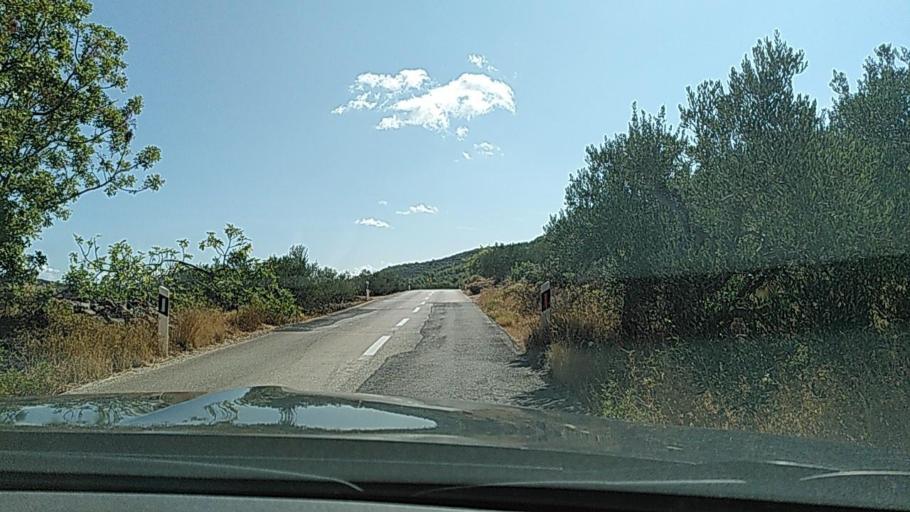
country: HR
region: Splitsko-Dalmatinska
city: Jelsa
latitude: 43.1441
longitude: 16.8091
